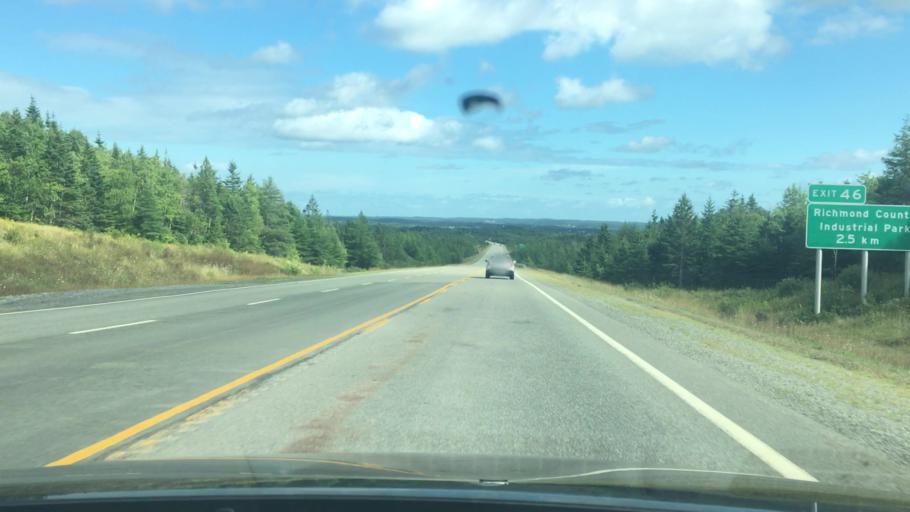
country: CA
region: Nova Scotia
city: Port Hawkesbury
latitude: 45.6206
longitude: -61.1159
